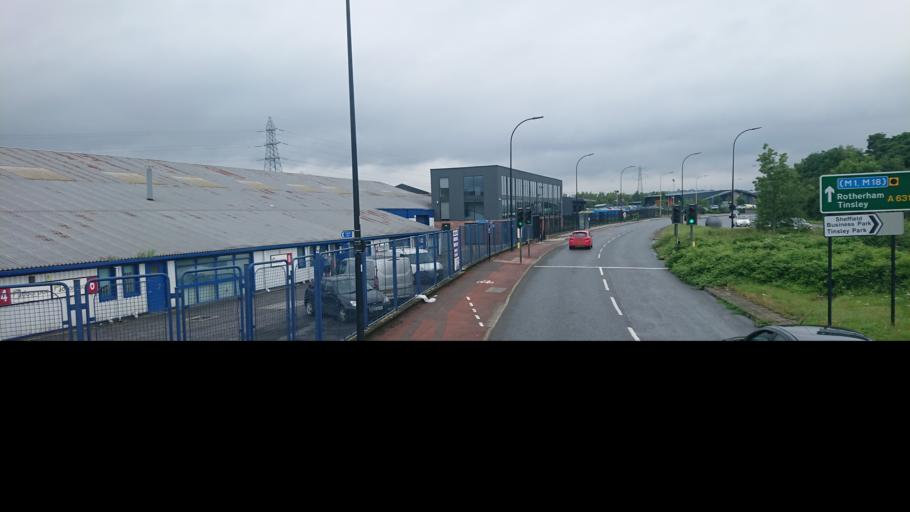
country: GB
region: England
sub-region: Rotherham
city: Orgreave
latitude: 53.4002
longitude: -1.4099
